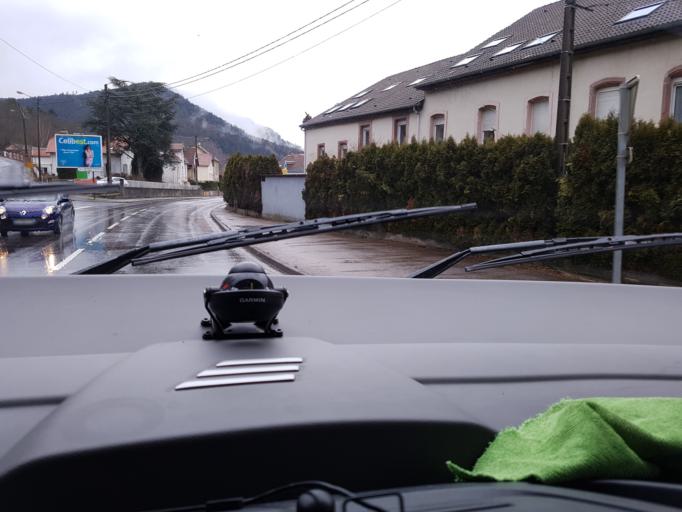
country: FR
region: Lorraine
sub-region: Departement des Vosges
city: Saint-Die-des-Vosges
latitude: 48.2864
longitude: 6.9306
